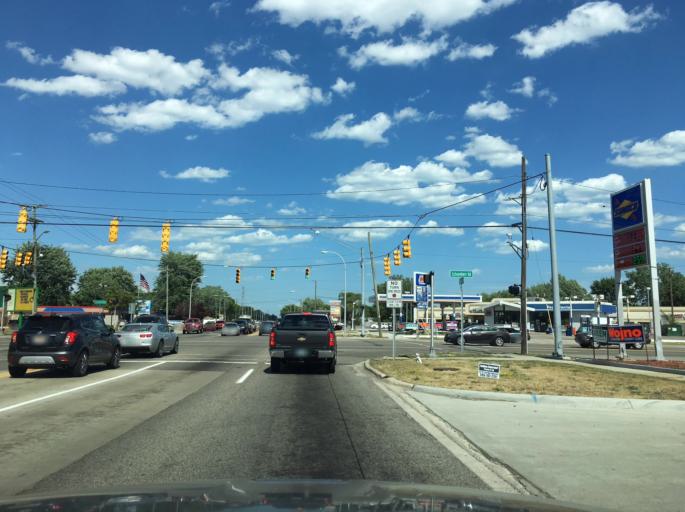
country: US
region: Michigan
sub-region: Macomb County
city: Center Line
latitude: 42.5076
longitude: -82.9878
